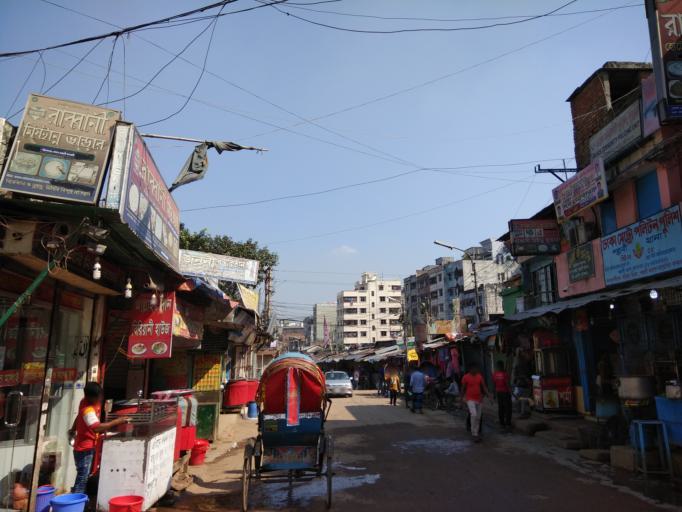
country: BD
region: Dhaka
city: Tungi
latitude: 23.8169
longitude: 90.3688
